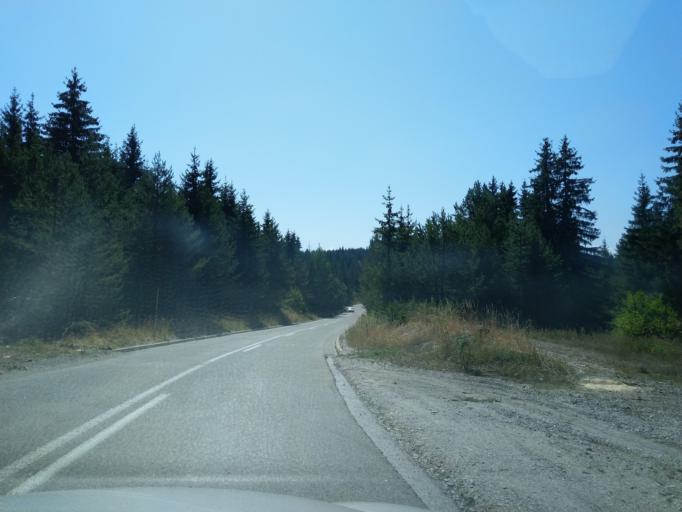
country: RS
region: Central Serbia
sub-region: Zlatiborski Okrug
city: Nova Varos
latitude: 43.3624
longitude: 19.8543
